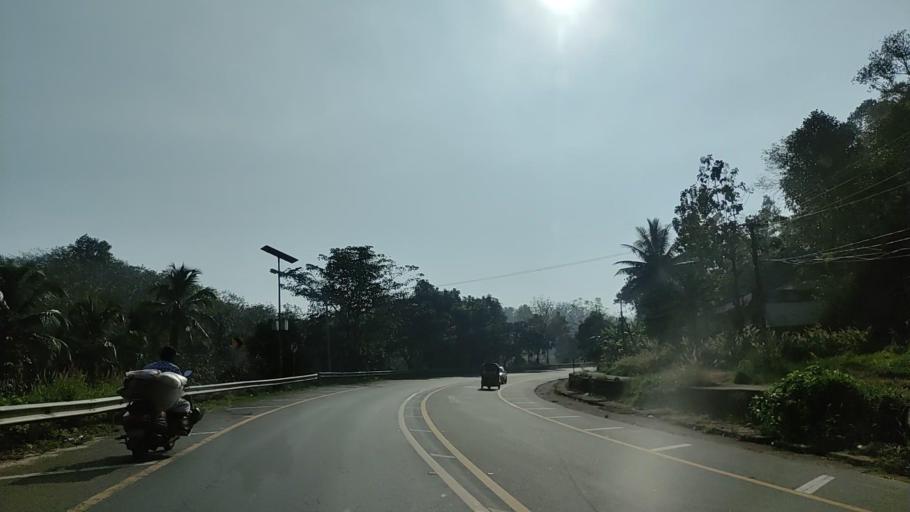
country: IN
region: Kerala
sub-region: Kollam
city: Punalur
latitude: 8.9670
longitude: 76.8332
